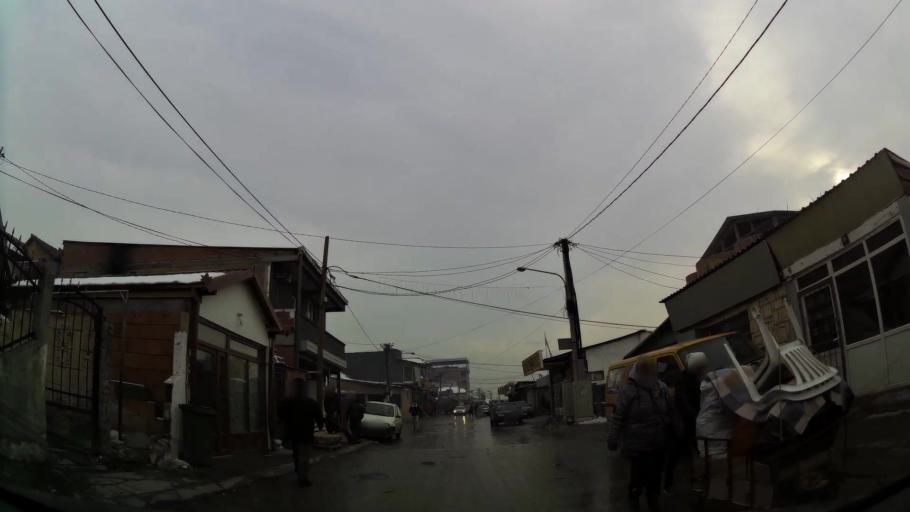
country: MK
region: Suto Orizari
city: Suto Orizare
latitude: 42.0433
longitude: 21.4233
